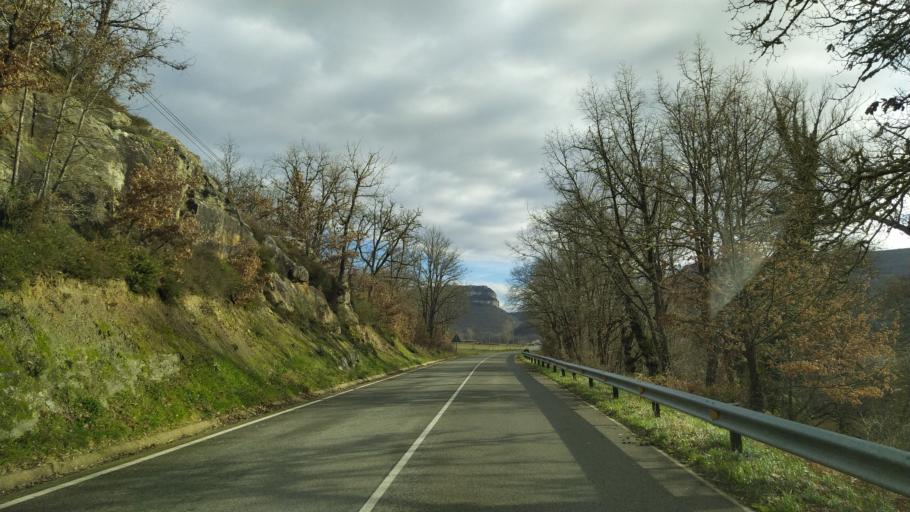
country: ES
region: Cantabria
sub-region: Provincia de Cantabria
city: San Martin de Elines
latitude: 42.8359
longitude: -3.8758
